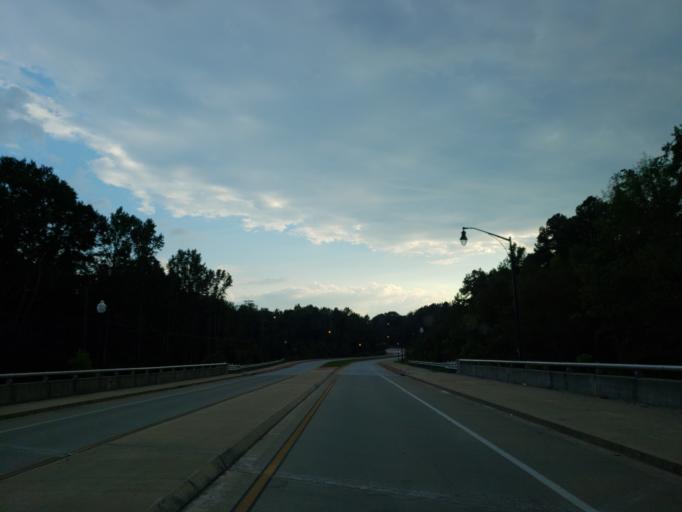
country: US
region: Georgia
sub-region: Cobb County
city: Powder Springs
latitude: 33.8501
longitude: -84.6836
